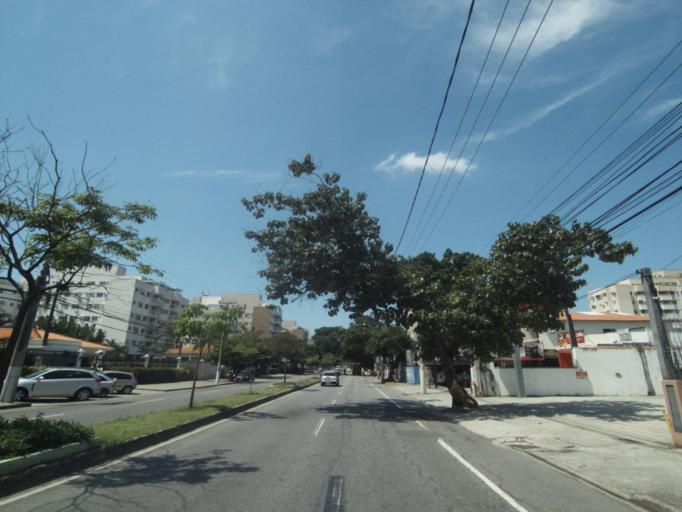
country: BR
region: Rio de Janeiro
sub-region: Niteroi
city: Niteroi
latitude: -22.9072
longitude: -43.0600
